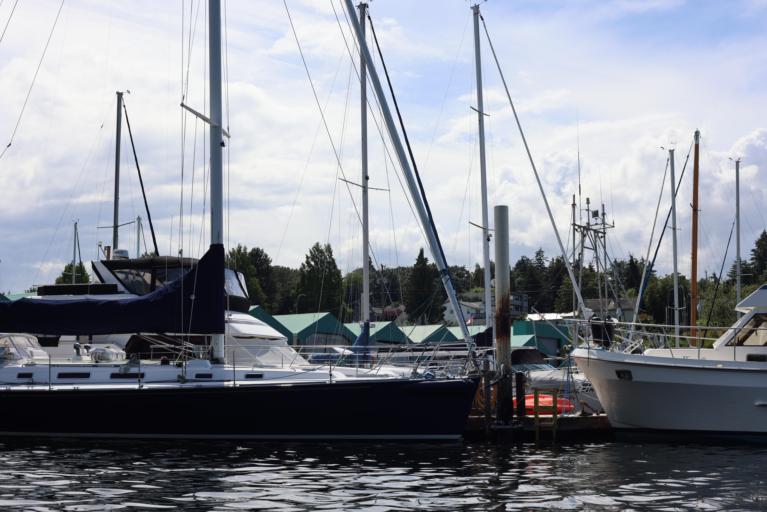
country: CA
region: British Columbia
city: Nanaimo
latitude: 49.1841
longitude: -123.9442
